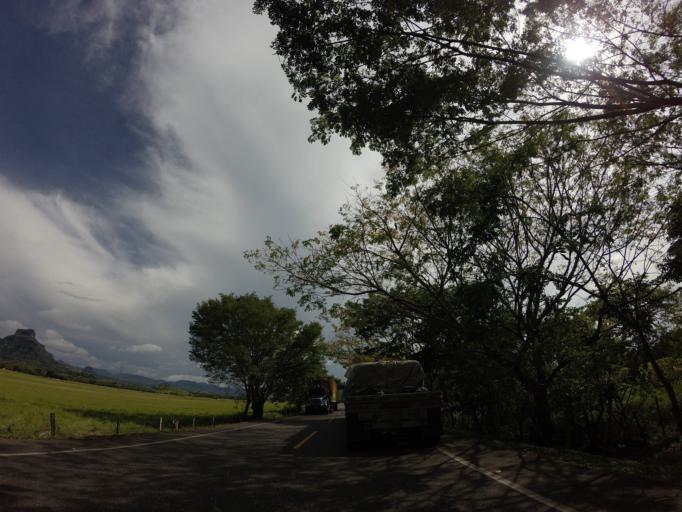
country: CO
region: Tolima
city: Honda
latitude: 5.3287
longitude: -74.7397
